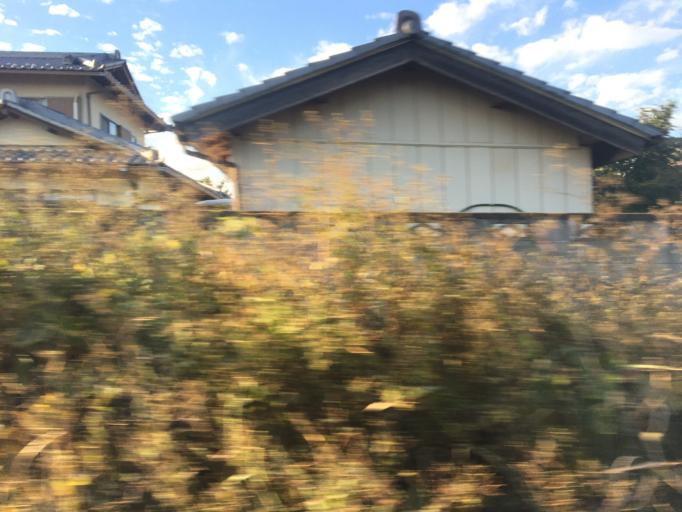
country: JP
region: Gunma
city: Kiryu
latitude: 36.4026
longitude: 139.3074
